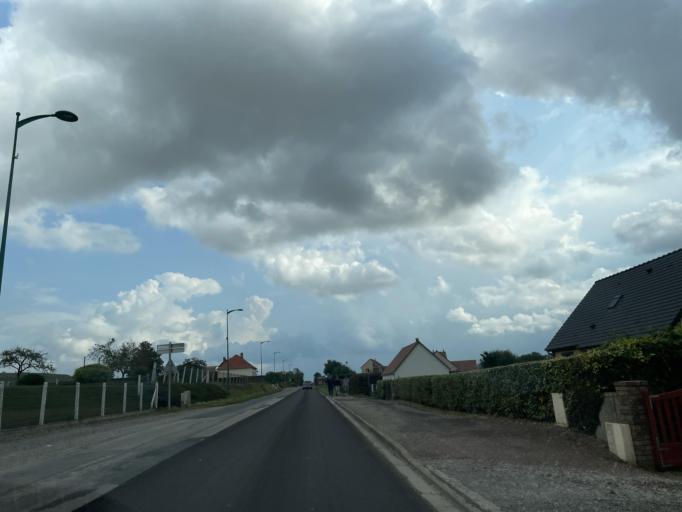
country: FR
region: Haute-Normandie
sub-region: Departement de la Seine-Maritime
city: Envermeu
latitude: 49.8693
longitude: 1.3248
